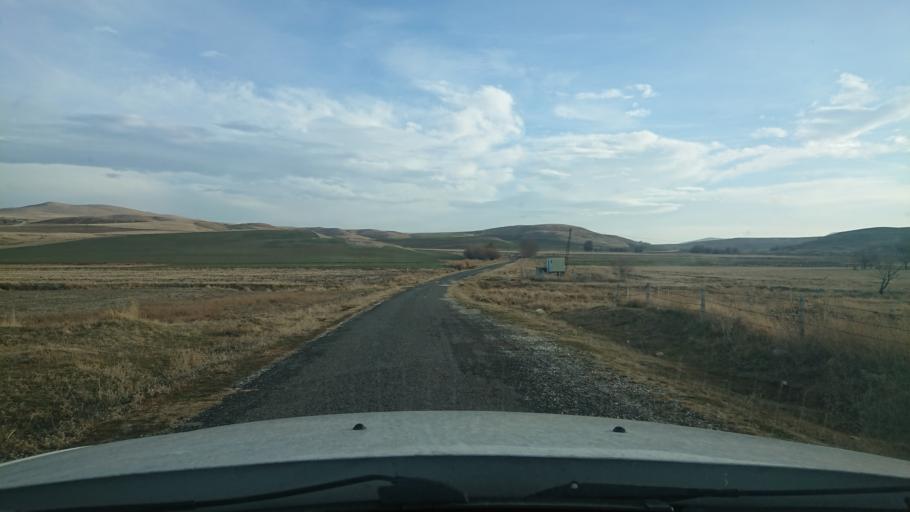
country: TR
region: Aksaray
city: Acipinar
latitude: 38.6828
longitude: 33.8631
